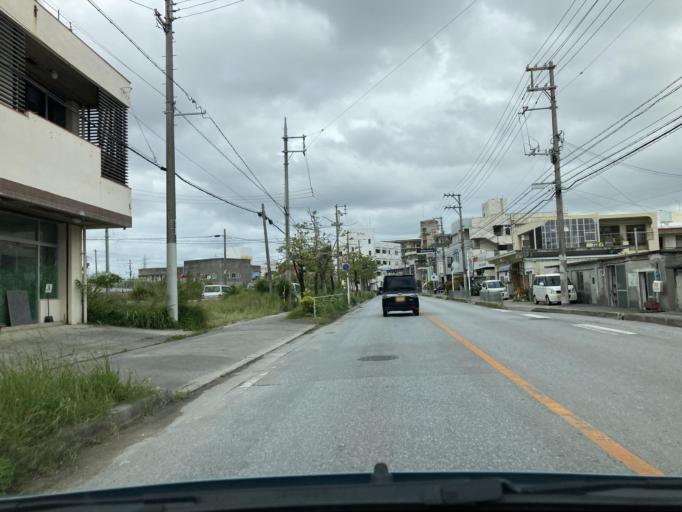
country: JP
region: Okinawa
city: Ginowan
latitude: 26.2372
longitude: 127.7498
